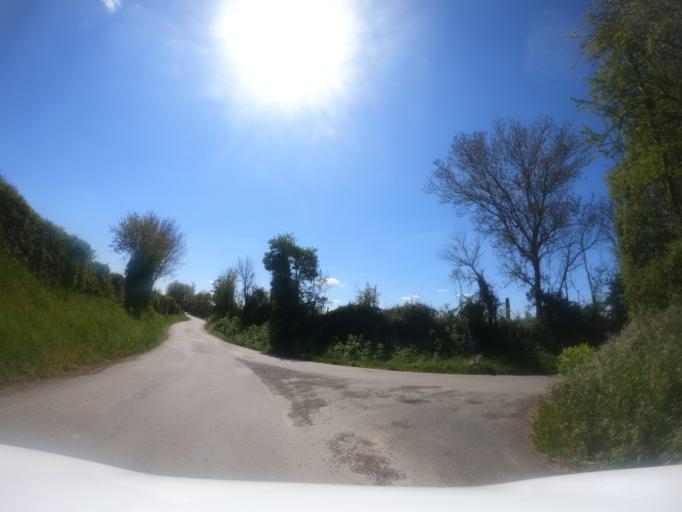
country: FR
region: Pays de la Loire
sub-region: Departement de la Vendee
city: Fontenay-le-Comte
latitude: 46.4412
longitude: -0.8724
